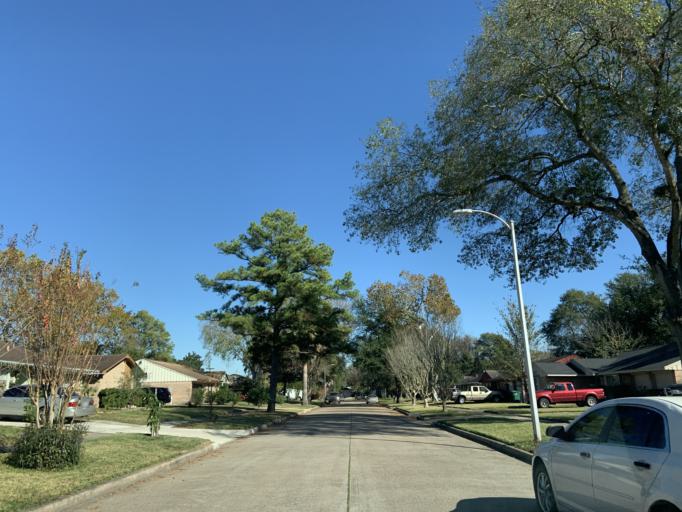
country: US
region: Texas
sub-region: Harris County
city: Bellaire
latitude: 29.6904
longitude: -95.5125
